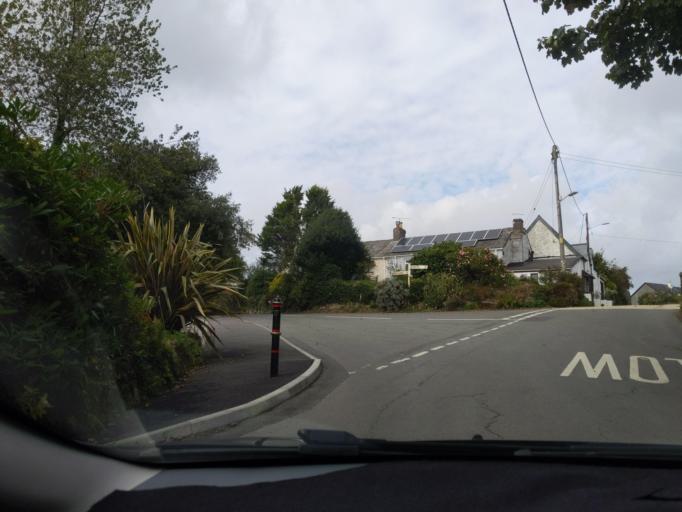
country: GB
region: England
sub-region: Cornwall
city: Lostwithiel
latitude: 50.3999
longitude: -4.7037
